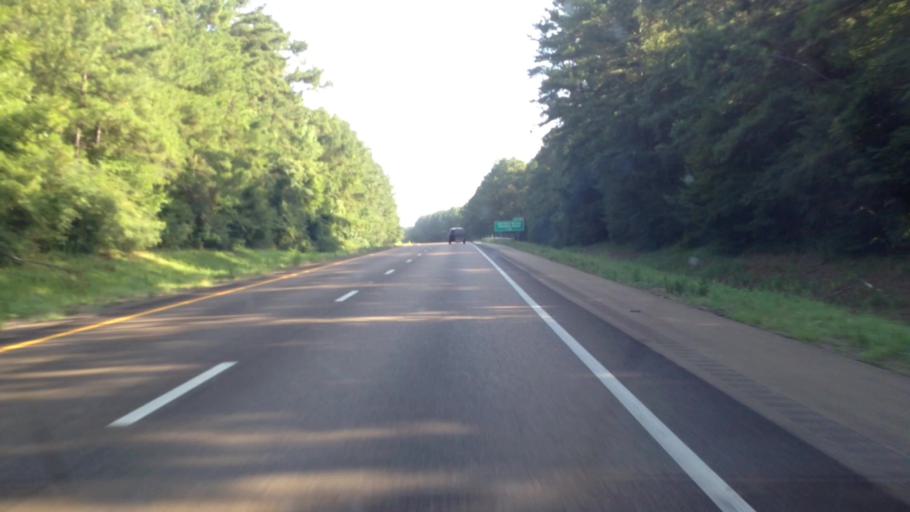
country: US
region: Mississippi
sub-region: Pike County
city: Summit
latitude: 31.3280
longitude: -90.4771
